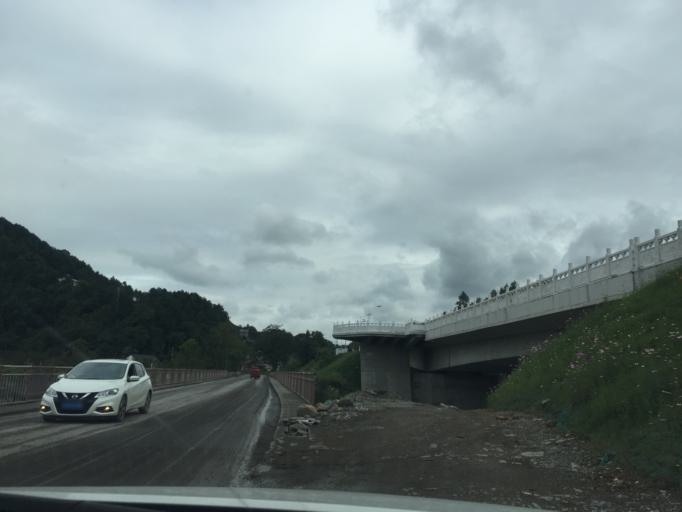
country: CN
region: Guizhou Sheng
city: Duyun
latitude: 26.3373
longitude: 107.5140
